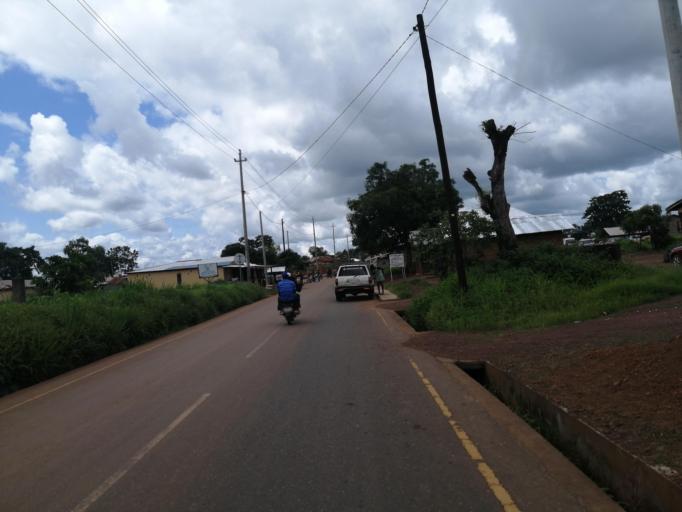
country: SL
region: Northern Province
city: Port Loko
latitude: 8.7724
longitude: -12.7759
